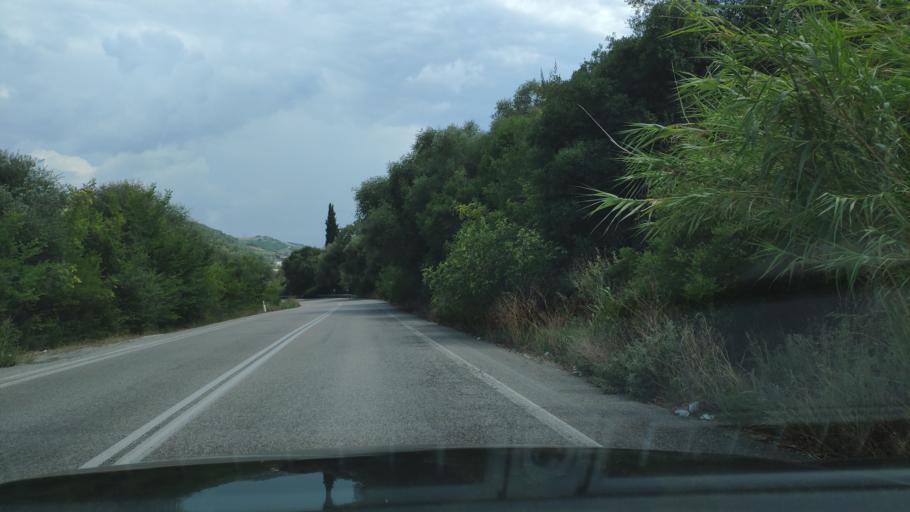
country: GR
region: West Greece
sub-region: Nomos Aitolias kai Akarnanias
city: Krikellos
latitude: 38.9913
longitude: 21.1564
